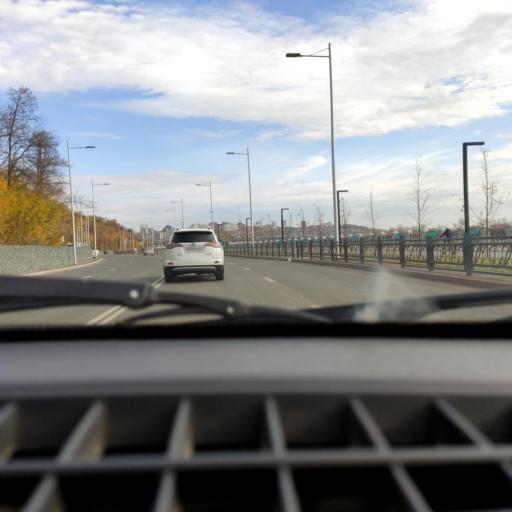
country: RU
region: Bashkortostan
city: Ufa
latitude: 54.7134
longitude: 55.9398
